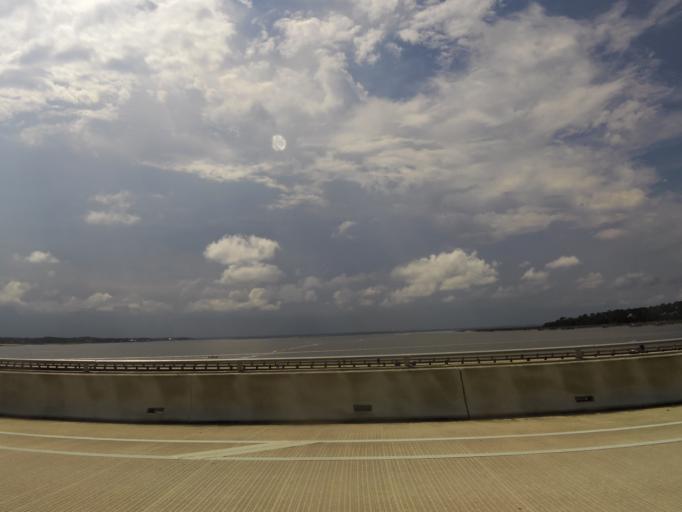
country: US
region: Florida
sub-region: Nassau County
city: Fernandina Beach
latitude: 30.5202
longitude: -81.4477
